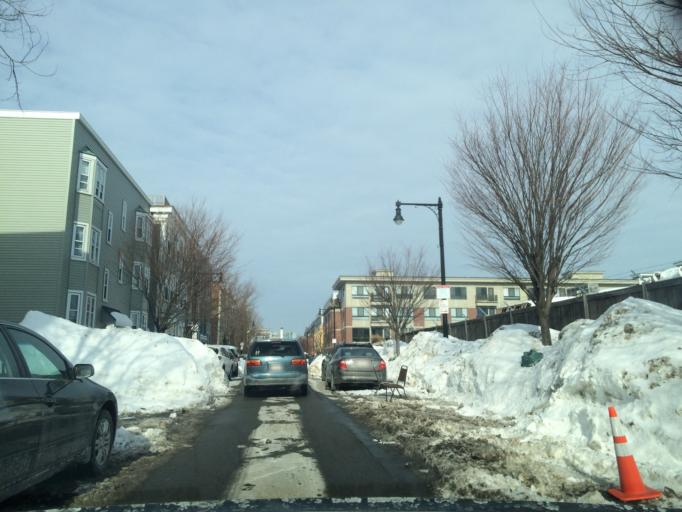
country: US
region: Massachusetts
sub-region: Suffolk County
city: South Boston
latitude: 42.3395
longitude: -71.0482
